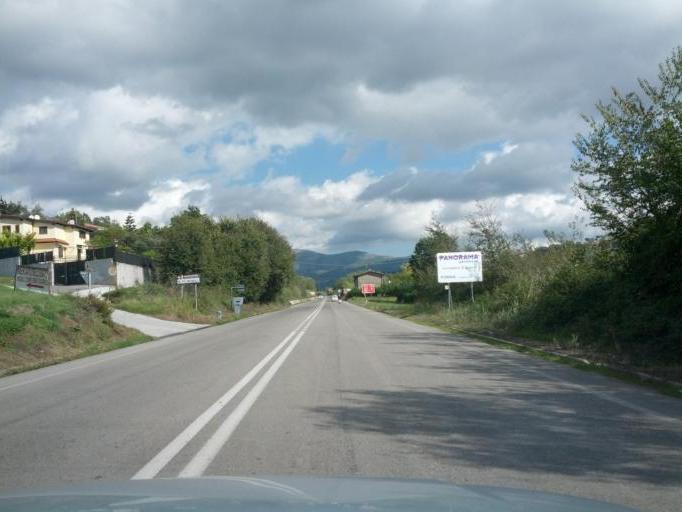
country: IT
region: Latium
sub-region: Provincia di Latina
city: Spigno Saturnia Inferiore
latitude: 41.2854
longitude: 13.7223
